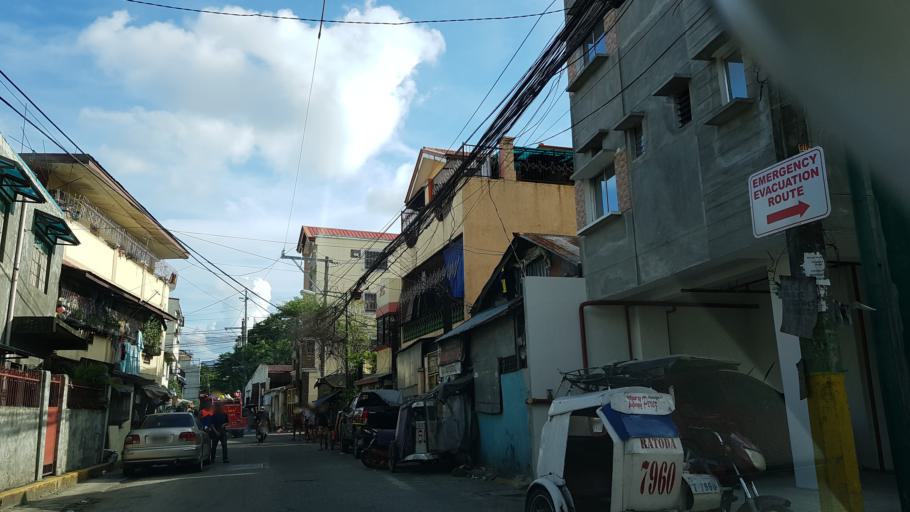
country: PH
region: Calabarzon
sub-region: Province of Rizal
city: Pateros
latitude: 14.5452
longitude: 121.0591
